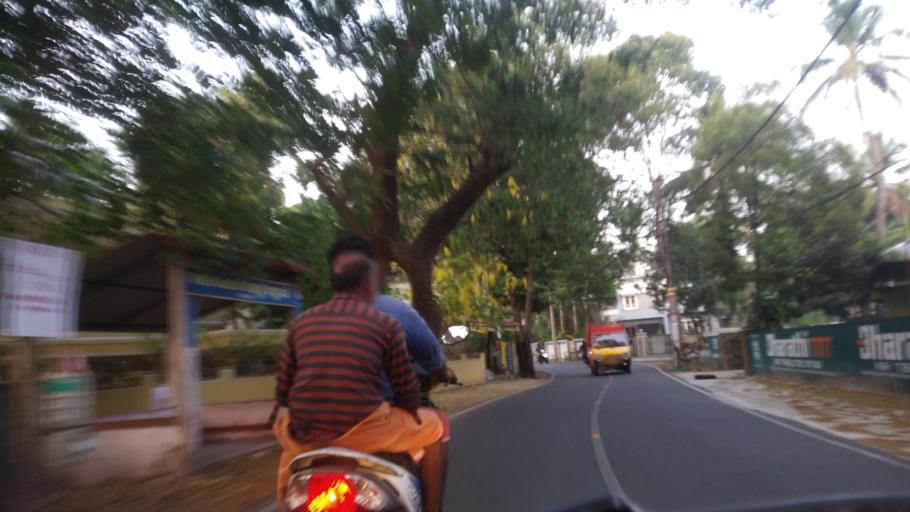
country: IN
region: Kerala
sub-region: Thrissur District
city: Kodungallur
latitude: 10.2050
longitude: 76.1806
